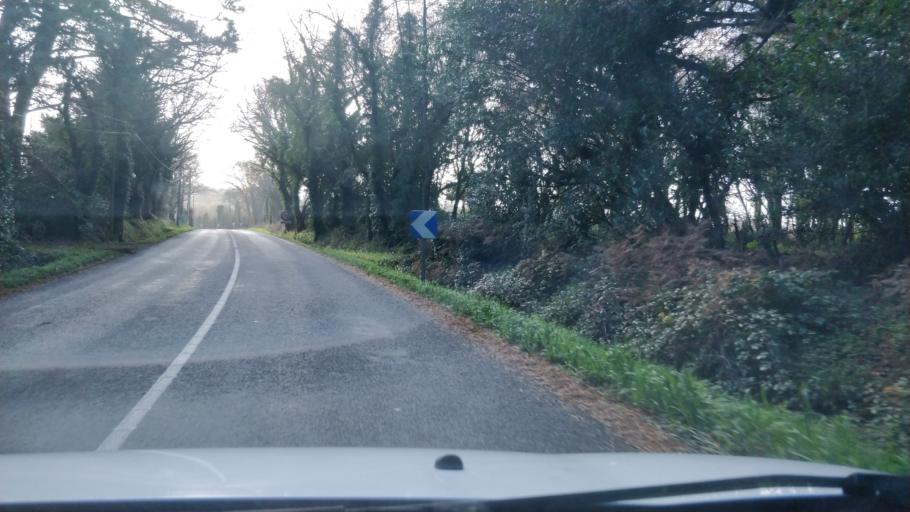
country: FR
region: Pays de la Loire
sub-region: Departement de la Loire-Atlantique
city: Saint-Molf
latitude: 47.3711
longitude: -2.4335
